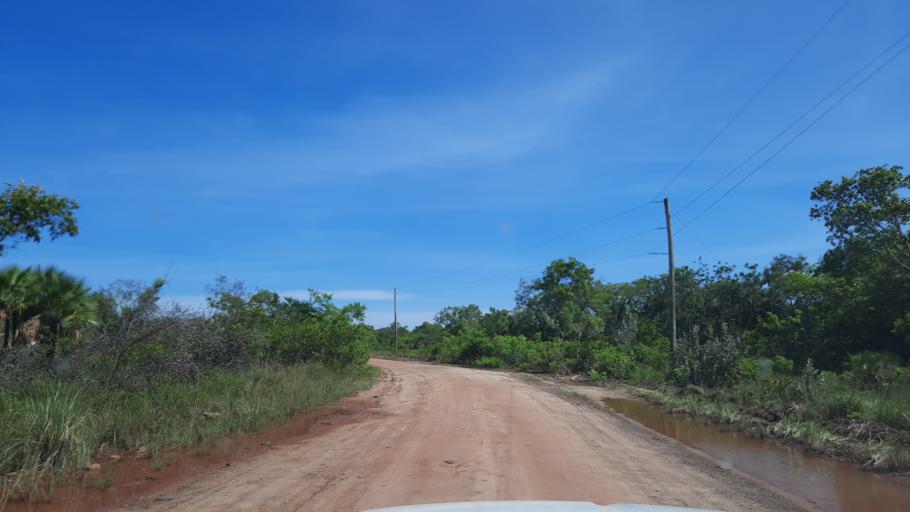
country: BZ
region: Stann Creek
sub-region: Dangriga
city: Dangriga
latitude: 17.1667
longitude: -88.3299
